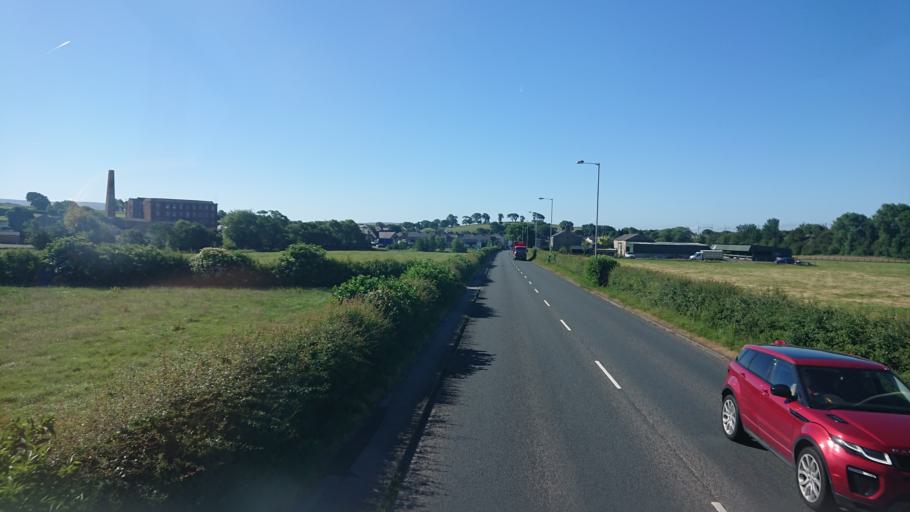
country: GB
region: England
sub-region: Lancashire
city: Galgate
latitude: 53.9972
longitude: -2.7905
